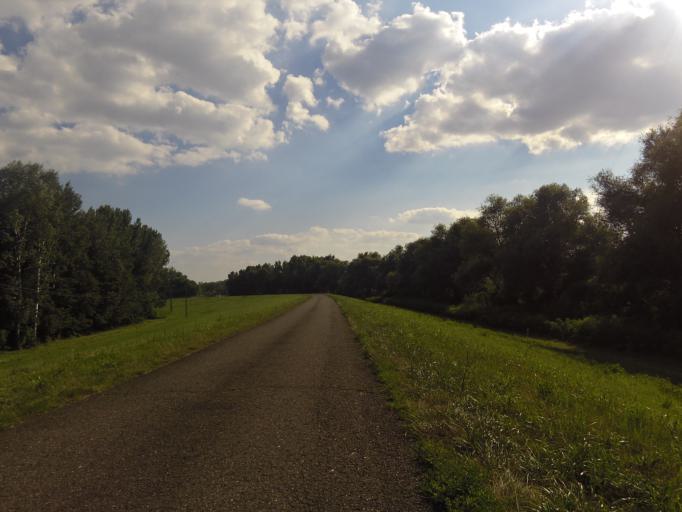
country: HU
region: Jasz-Nagykun-Szolnok
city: Abadszalok
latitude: 47.5160
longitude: 20.5875
